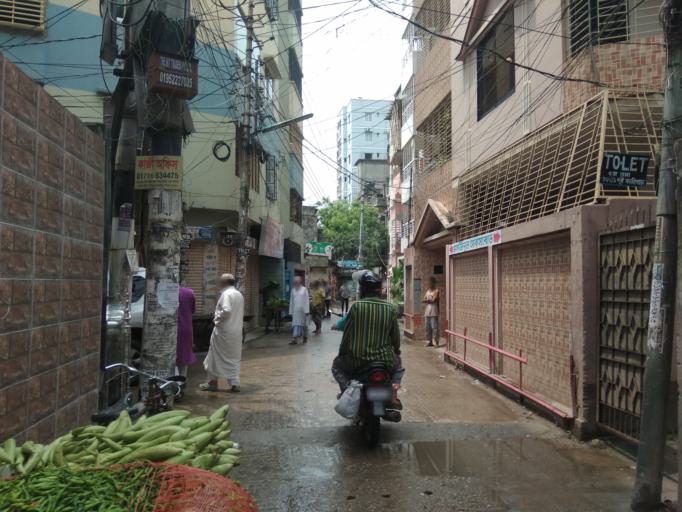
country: BD
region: Dhaka
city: Azimpur
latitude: 23.7991
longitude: 90.3742
